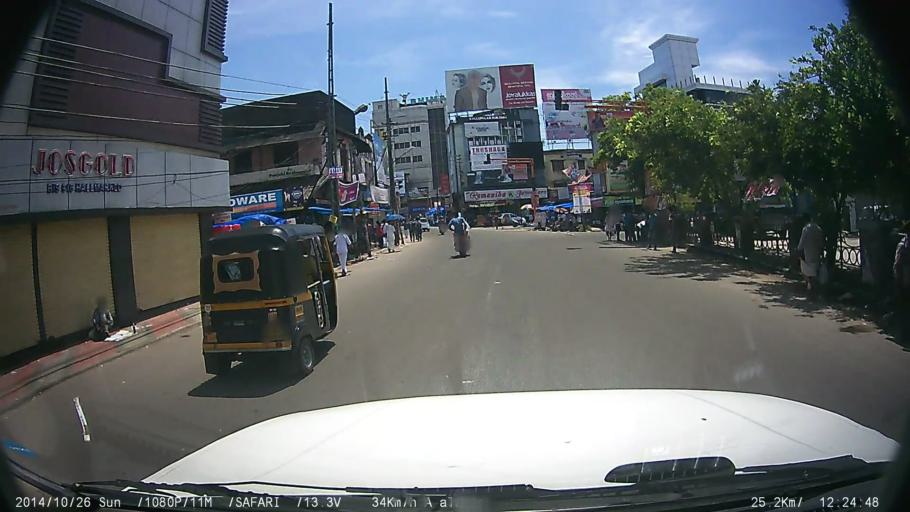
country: IN
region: Kerala
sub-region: Kottayam
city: Kottayam
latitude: 9.5895
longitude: 76.5224
